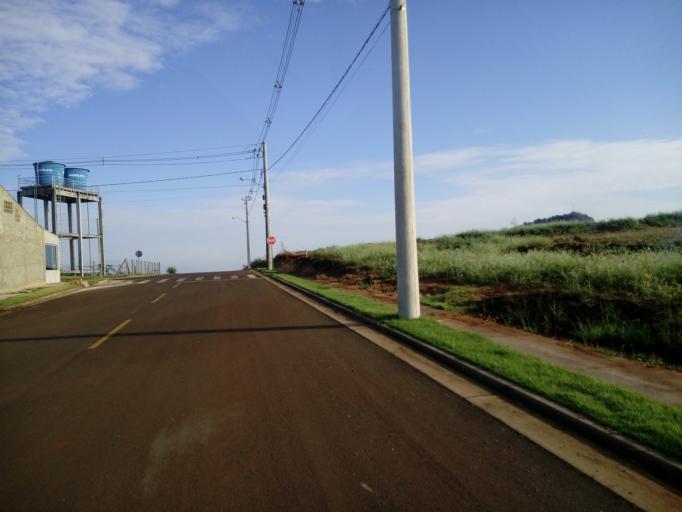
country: BR
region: Santa Catarina
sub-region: Chapeco
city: Chapeco
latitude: -27.0888
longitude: -52.7102
